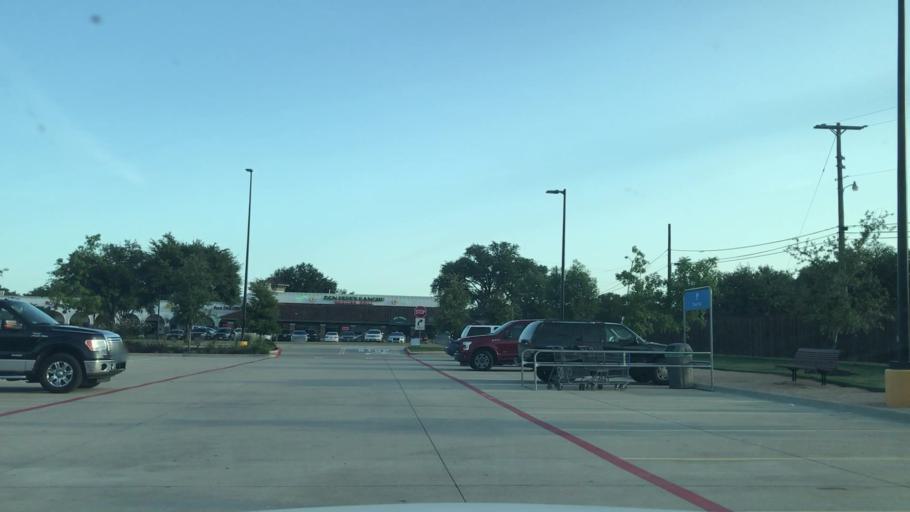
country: US
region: Texas
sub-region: Dallas County
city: Richardson
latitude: 32.9628
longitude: -96.7709
